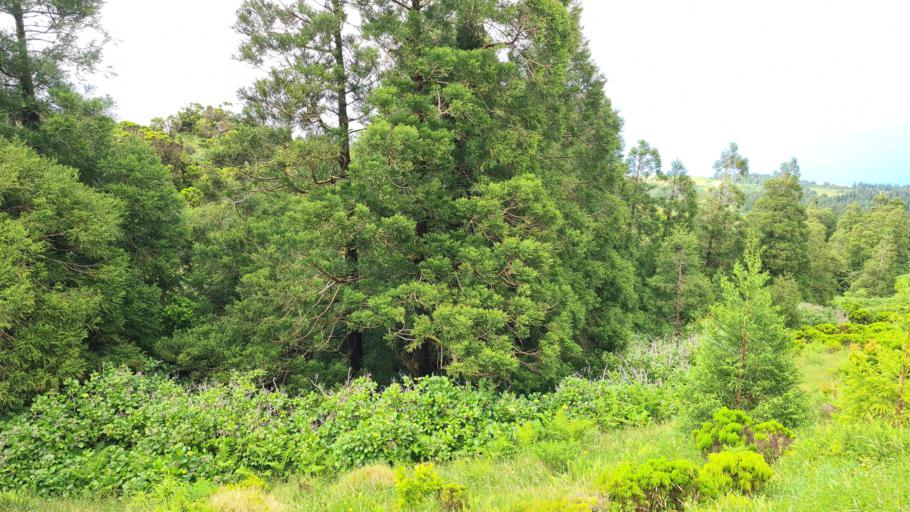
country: PT
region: Azores
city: Ribeira Grande
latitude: 38.5968
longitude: -28.7093
